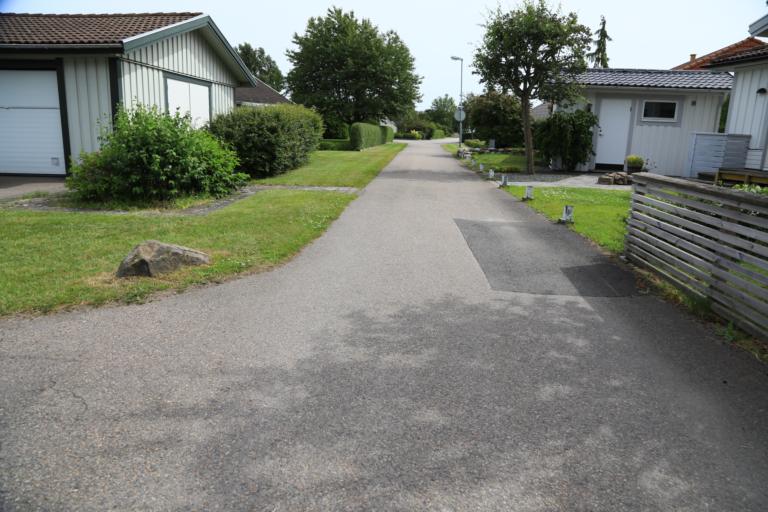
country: SE
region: Halland
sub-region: Varbergs Kommun
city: Varberg
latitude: 57.1085
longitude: 12.2944
